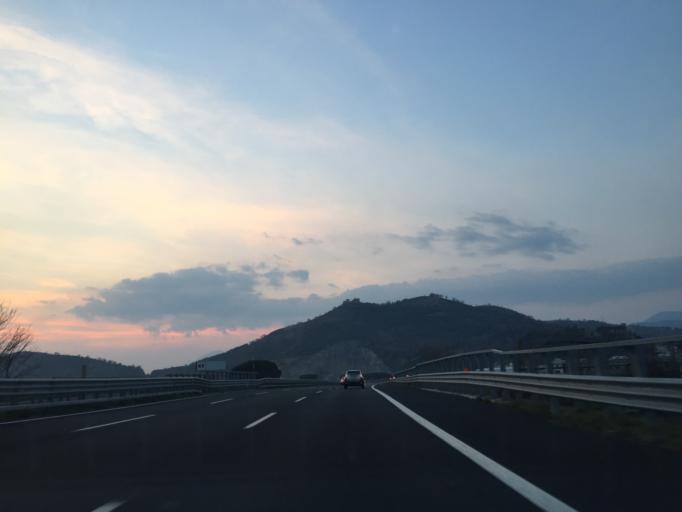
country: IT
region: Campania
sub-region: Provincia di Salerno
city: Casali-San Potito
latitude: 40.7685
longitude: 14.6748
